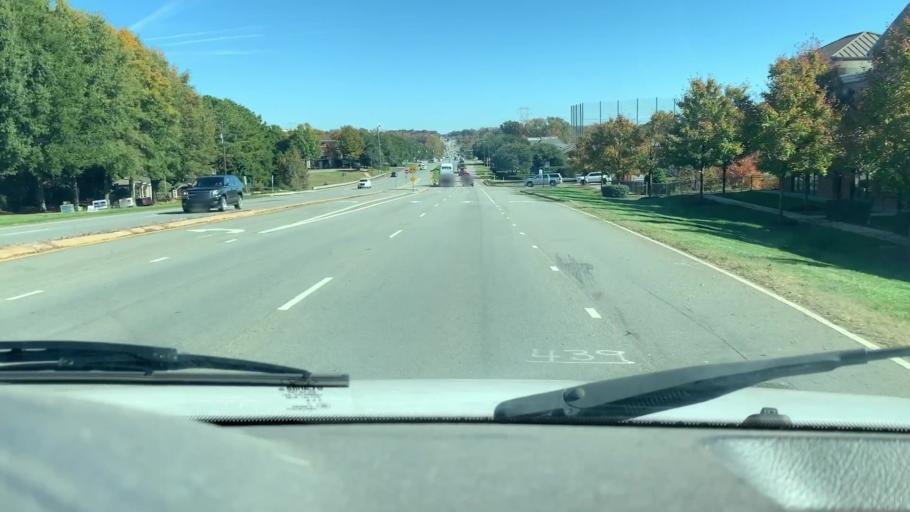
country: US
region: North Carolina
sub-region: Mecklenburg County
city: Cornelius
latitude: 35.4438
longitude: -80.8864
